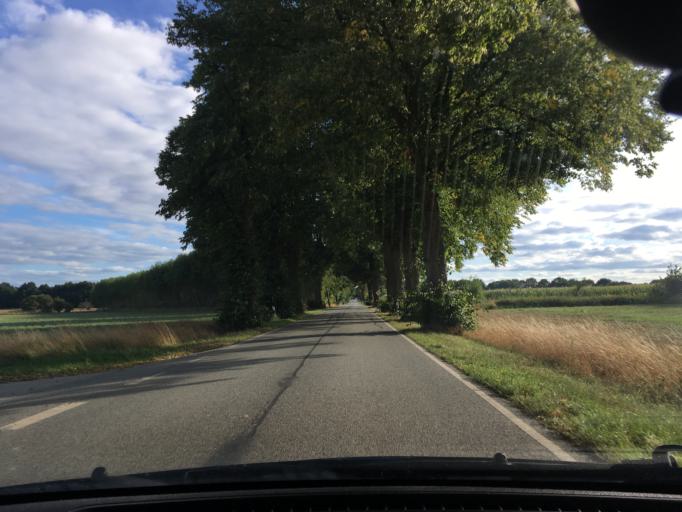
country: DE
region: Lower Saxony
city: Brackel
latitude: 53.3093
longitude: 10.0526
